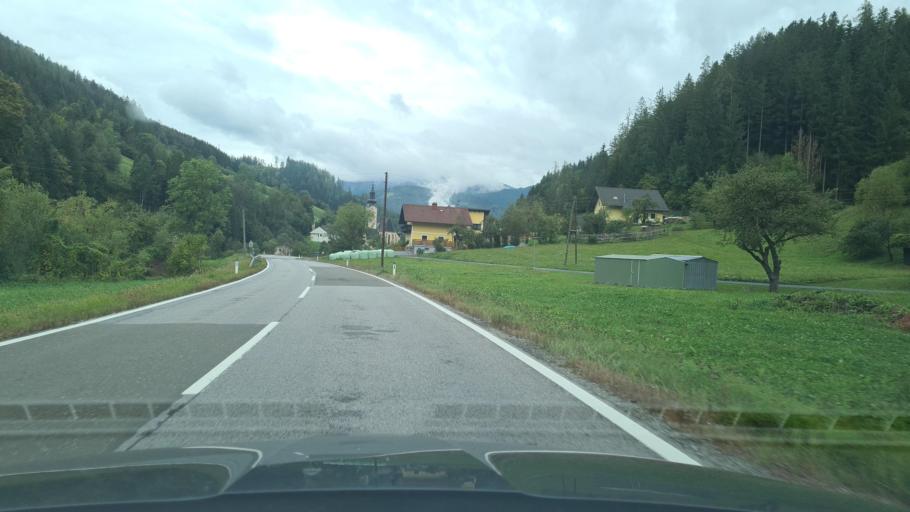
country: AT
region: Styria
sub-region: Politischer Bezirk Bruck-Muerzzuschlag
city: Allerheiligen im Muerztal
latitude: 47.3853
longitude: 15.4617
